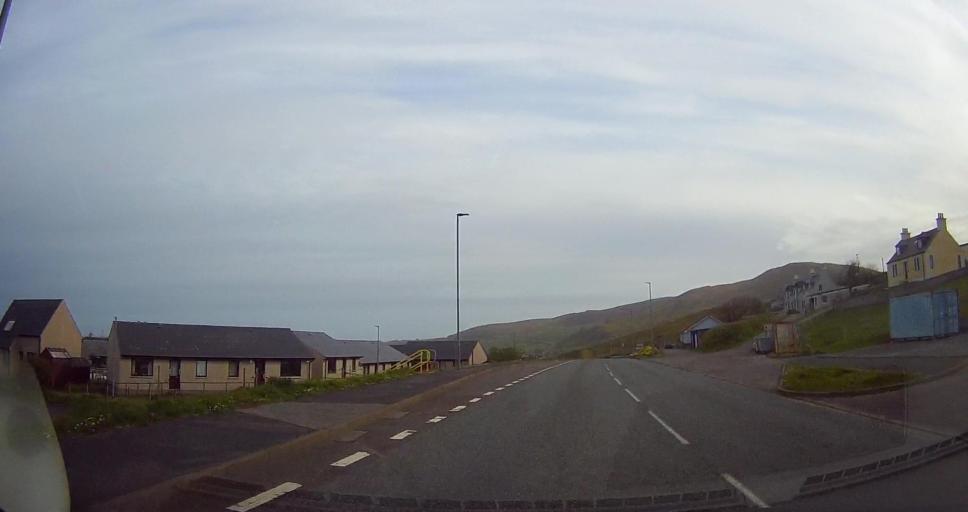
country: GB
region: Scotland
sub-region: Shetland Islands
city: Sandwick
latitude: 60.0460
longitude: -1.2277
